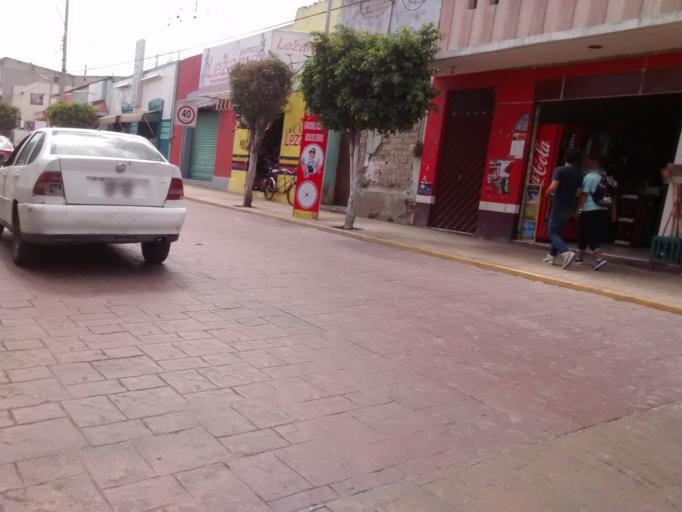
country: MX
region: Puebla
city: Tehuacan
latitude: 18.4607
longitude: -97.3872
